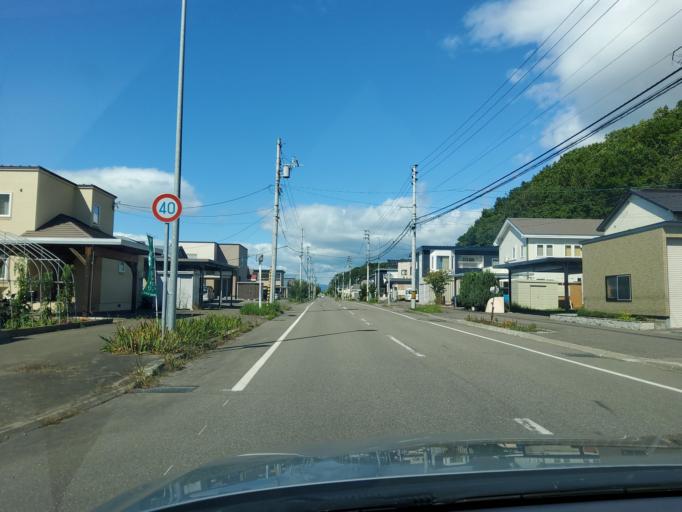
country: JP
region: Hokkaido
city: Obihiro
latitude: 42.9411
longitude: 143.2233
